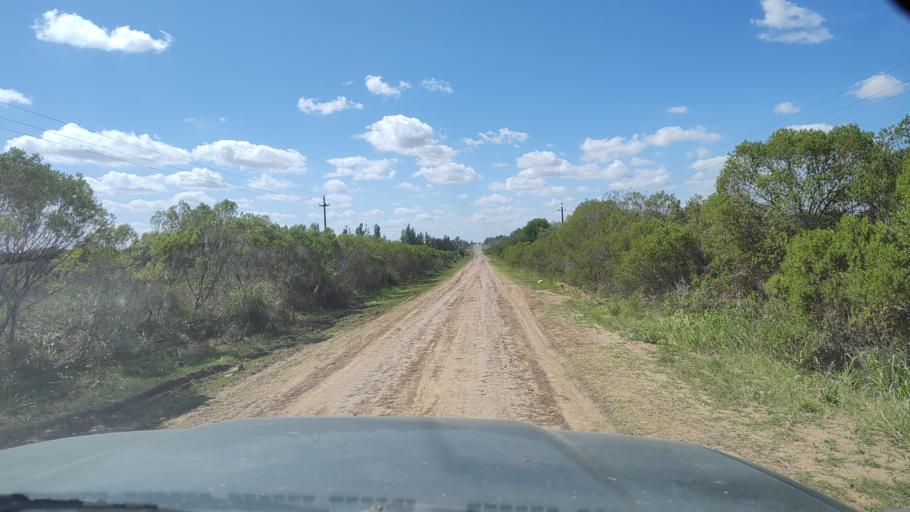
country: AR
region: Buenos Aires
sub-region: Partido de Lujan
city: Lujan
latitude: -34.5369
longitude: -59.1461
